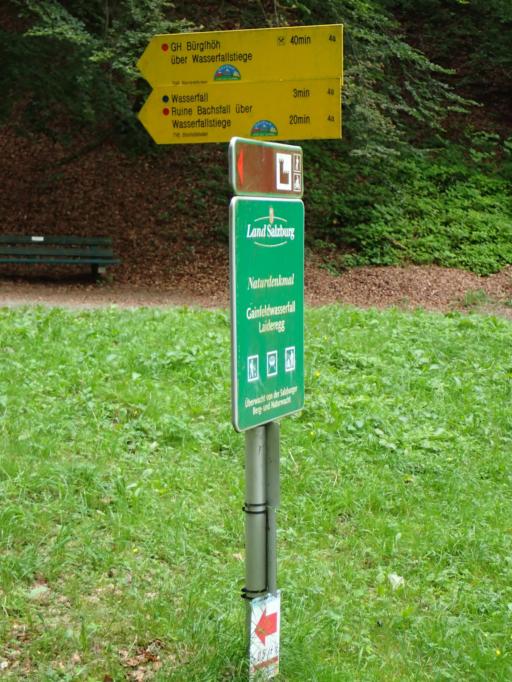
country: AT
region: Salzburg
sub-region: Politischer Bezirk Sankt Johann im Pongau
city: Bischofshofen
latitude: 47.4115
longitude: 13.2071
